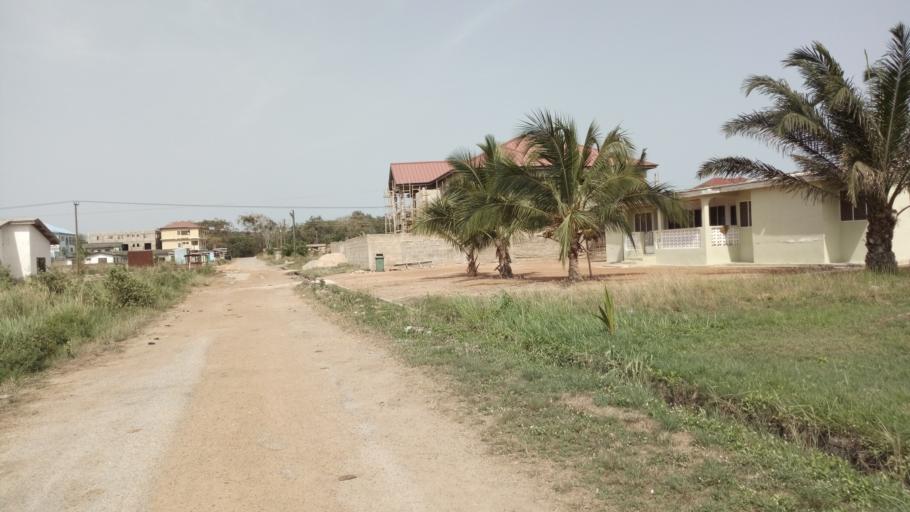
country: GH
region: Central
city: Winneba
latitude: 5.3626
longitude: -0.6374
